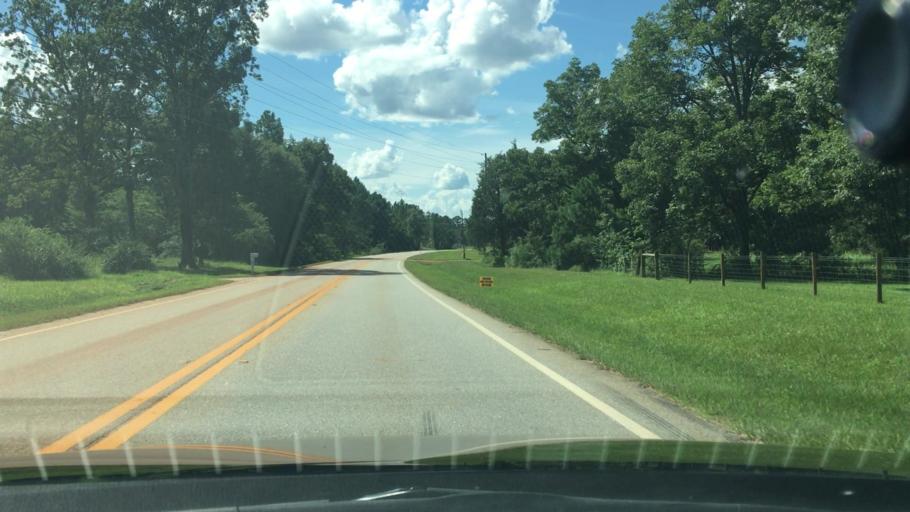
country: US
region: Georgia
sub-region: Jasper County
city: Monticello
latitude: 33.3027
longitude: -83.7295
